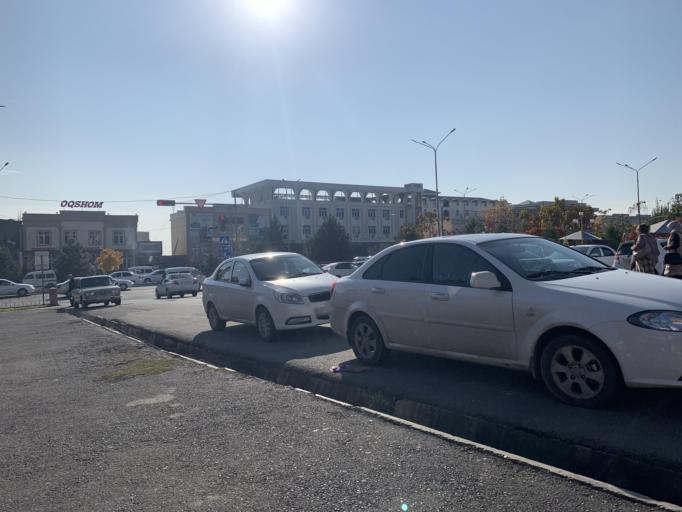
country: UZ
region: Namangan
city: Namangan Shahri
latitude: 40.9963
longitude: 71.5905
